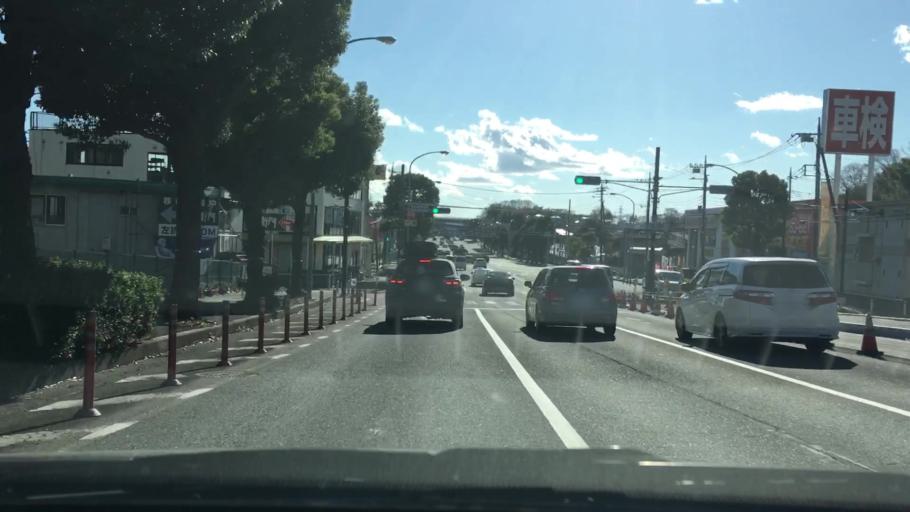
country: JP
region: Kanagawa
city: Yokohama
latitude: 35.5311
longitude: 139.5930
